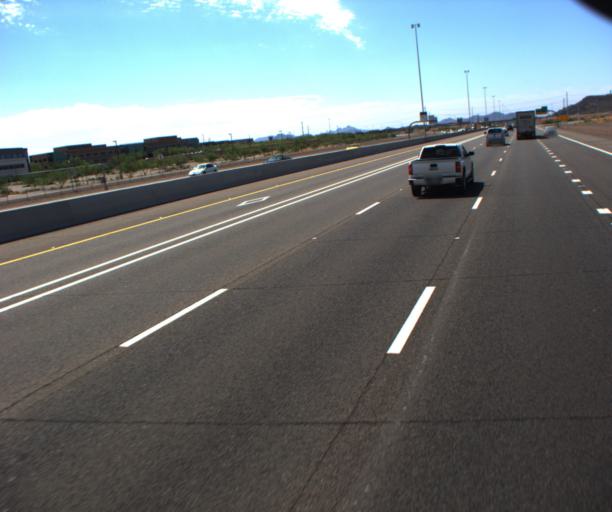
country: US
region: Arizona
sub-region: Maricopa County
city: Anthem
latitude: 33.7201
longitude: -112.1192
